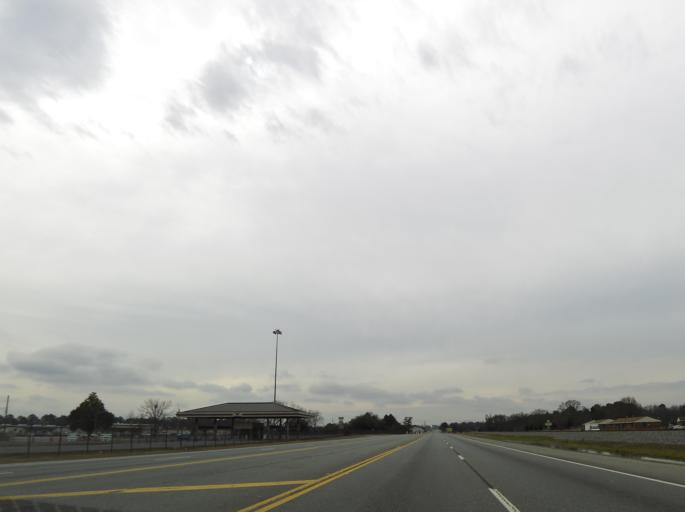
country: US
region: Georgia
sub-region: Houston County
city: Warner Robins
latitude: 32.6123
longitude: -83.5971
